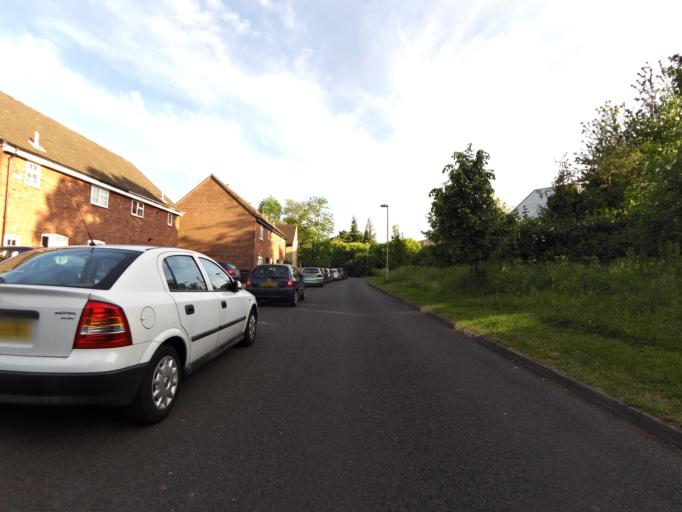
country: GB
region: England
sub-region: Norfolk
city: Norwich
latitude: 52.6611
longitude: 1.2886
